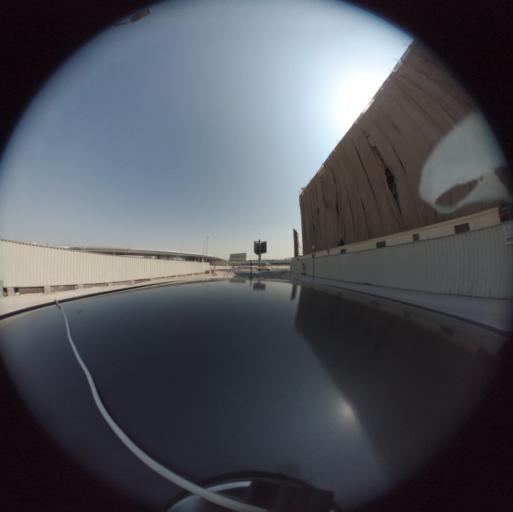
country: AE
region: Dubai
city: Dubai
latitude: 25.1593
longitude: 55.2284
